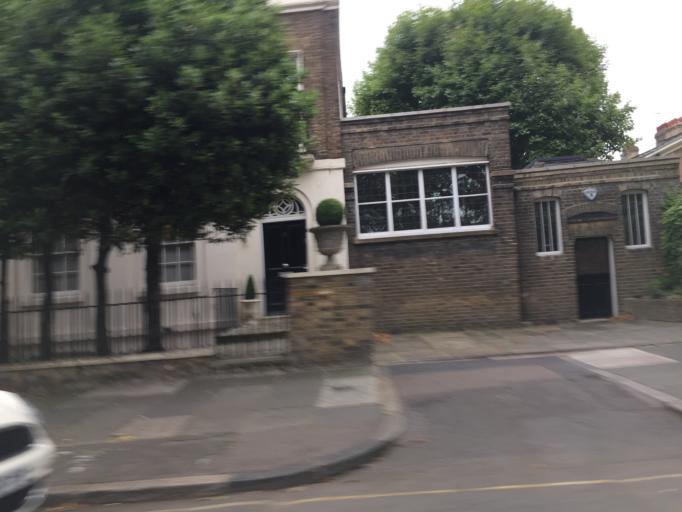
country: GB
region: England
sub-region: Greater London
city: Bayswater
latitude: 51.5264
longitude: -0.1754
